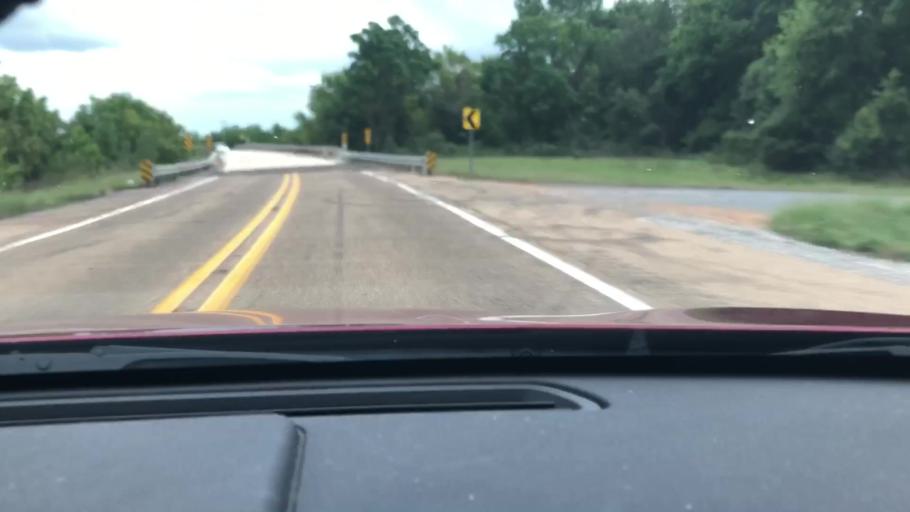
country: US
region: Arkansas
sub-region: Miller County
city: Texarkana
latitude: 33.4136
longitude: -93.8086
